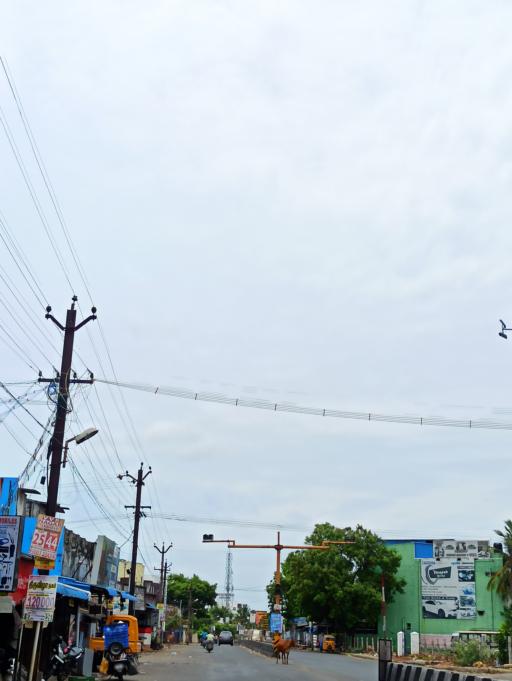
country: IN
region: Tamil Nadu
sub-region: Kancheepuram
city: Vandalur
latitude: 12.9190
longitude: 80.0834
